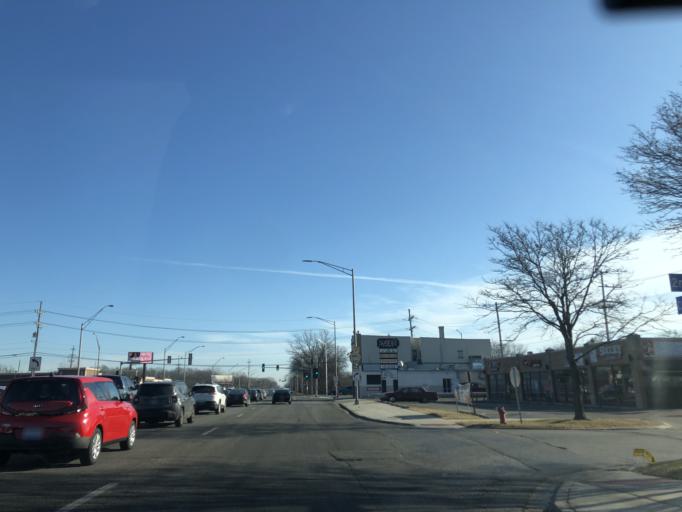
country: US
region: Illinois
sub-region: Cook County
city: North Riverside
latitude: 41.8497
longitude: -87.8343
